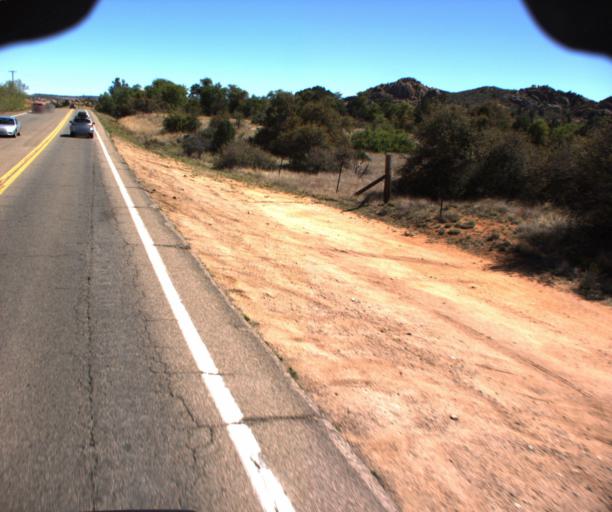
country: US
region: Arizona
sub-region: Yavapai County
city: Prescott
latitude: 34.6211
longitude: -112.4253
